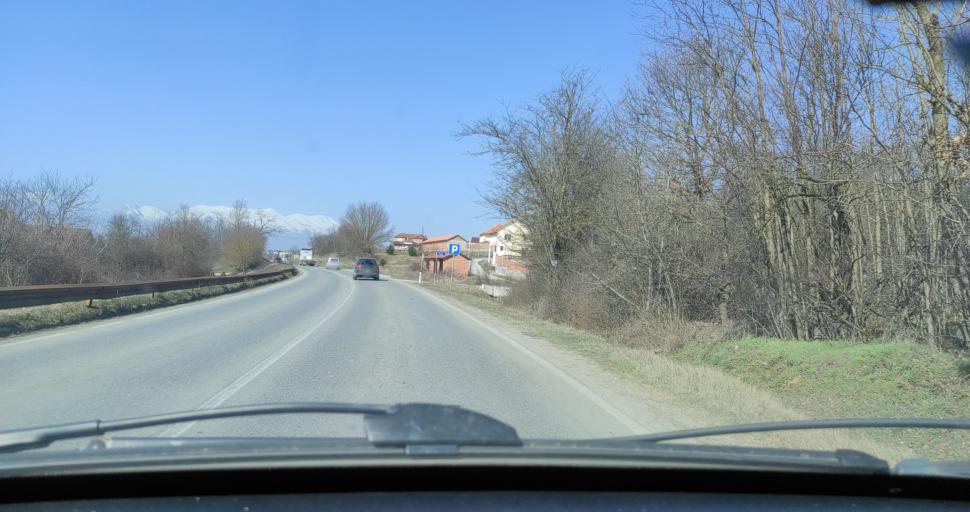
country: XK
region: Pec
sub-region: Komuna e Pejes
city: Kosuriq
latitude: 42.6107
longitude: 20.5054
